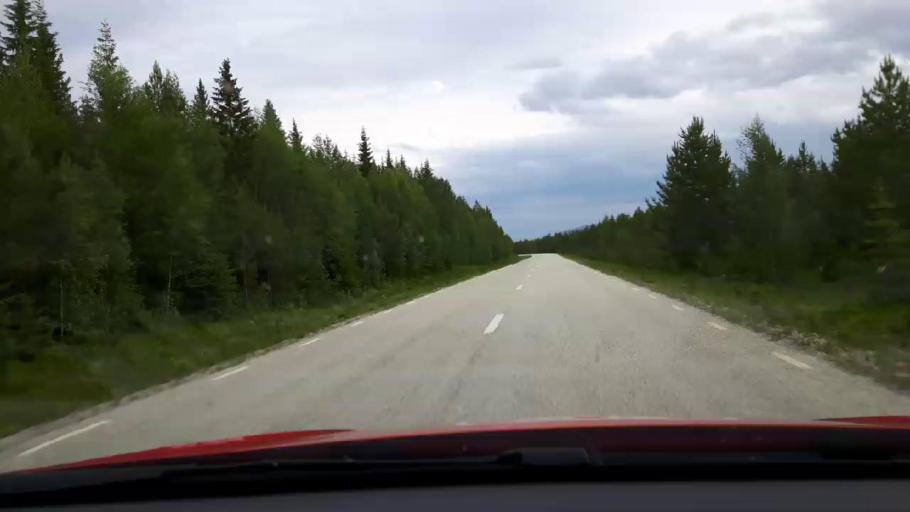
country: SE
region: Jaemtland
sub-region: Bergs Kommun
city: Hoverberg
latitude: 62.7117
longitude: 13.9305
